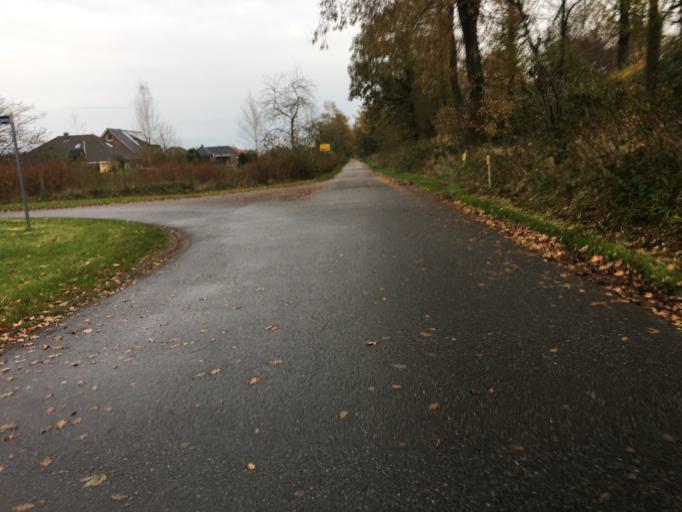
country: DE
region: Schleswig-Holstein
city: Wanderup
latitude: 54.6903
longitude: 9.3408
